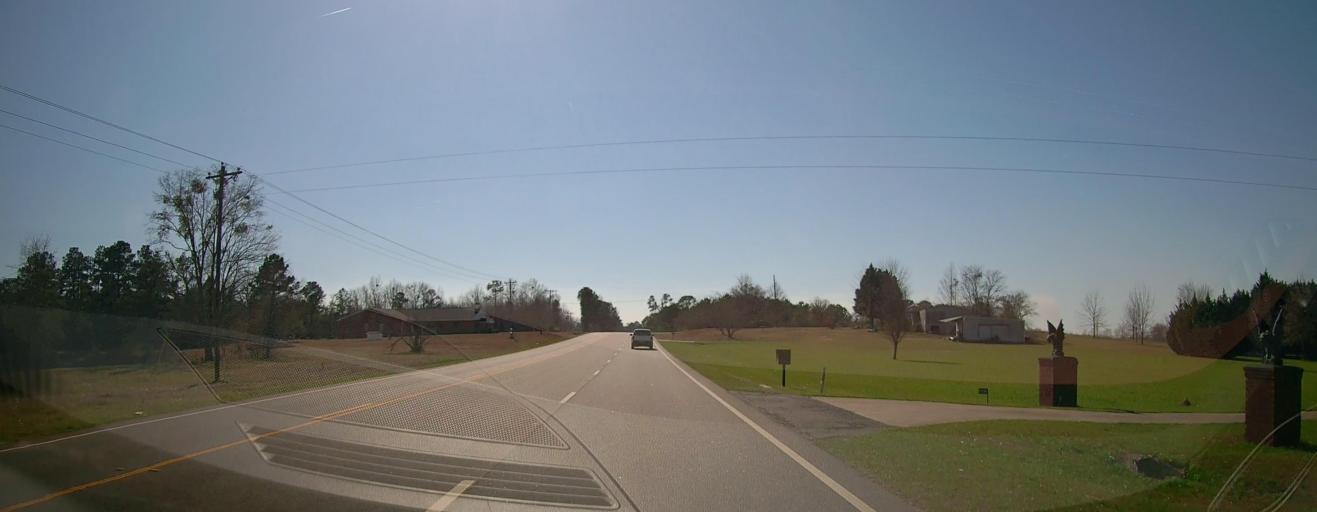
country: US
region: Georgia
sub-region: Macon County
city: Montezuma
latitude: 32.3223
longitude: -83.8850
